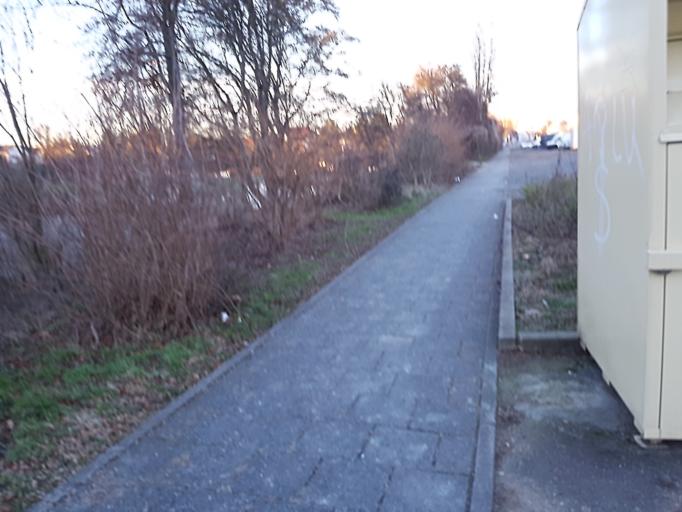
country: DE
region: Hesse
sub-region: Regierungsbezirk Darmstadt
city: Florsheim
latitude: 50.0071
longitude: 8.4206
